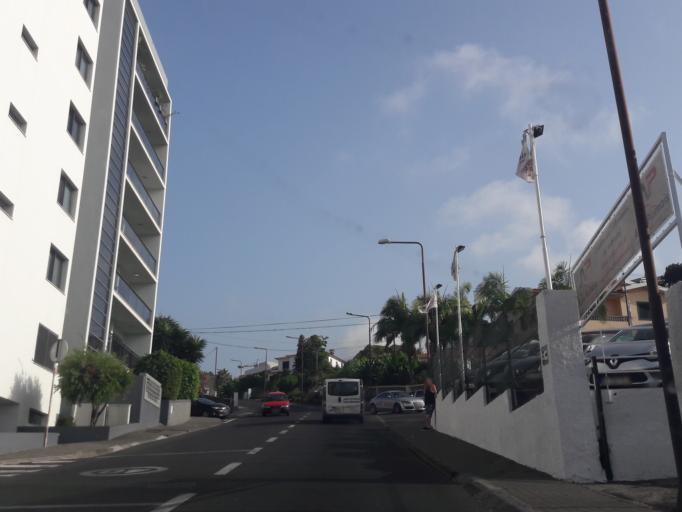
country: PT
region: Madeira
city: Camara de Lobos
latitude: 32.6413
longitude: -16.9446
